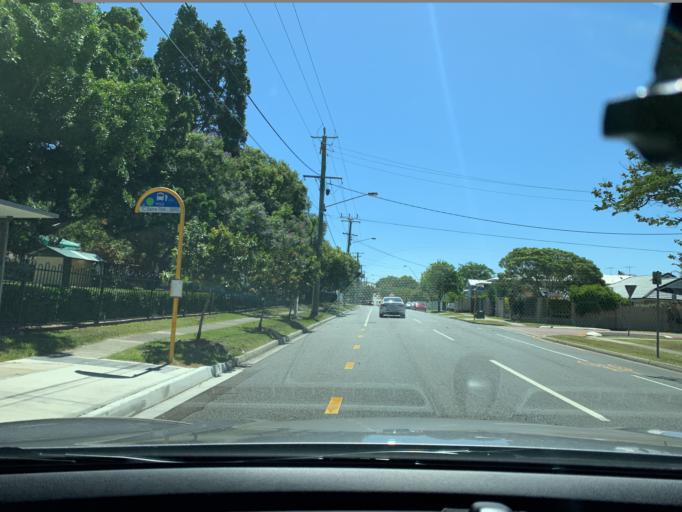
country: AU
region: Queensland
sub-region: Brisbane
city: Ascot
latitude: -27.4187
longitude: 153.0695
